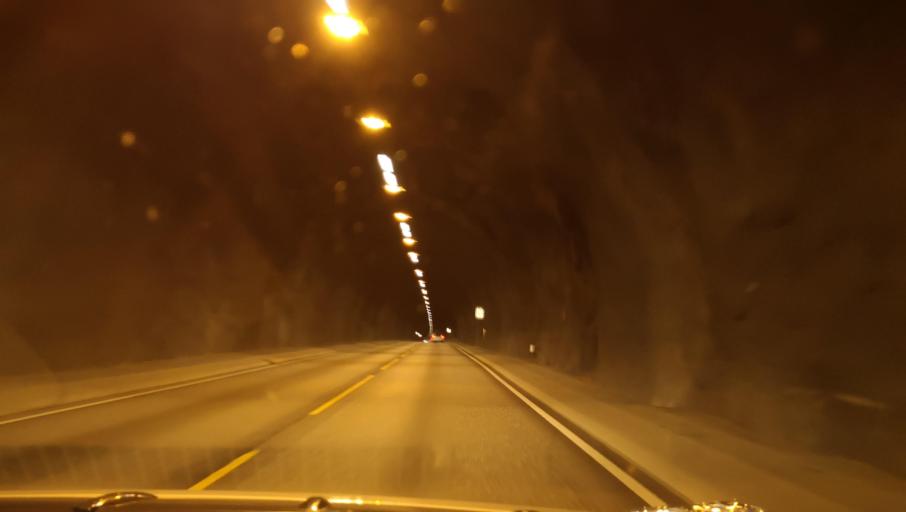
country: NO
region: Hordaland
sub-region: Granvin
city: Granvin
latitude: 60.5840
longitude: 6.6173
